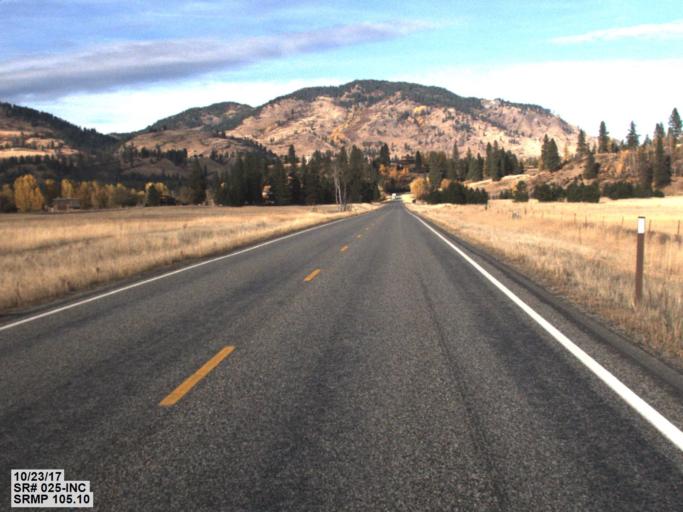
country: CA
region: British Columbia
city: Rossland
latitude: 48.8426
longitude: -117.9014
